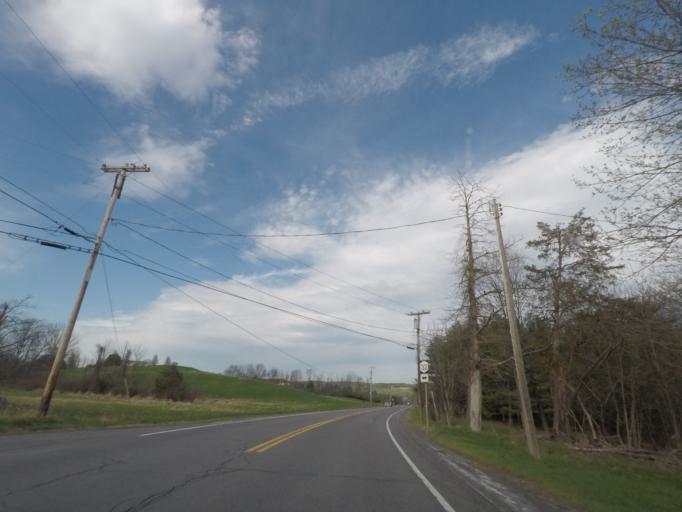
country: US
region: New York
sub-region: Albany County
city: Voorheesville
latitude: 42.5664
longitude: -73.9278
